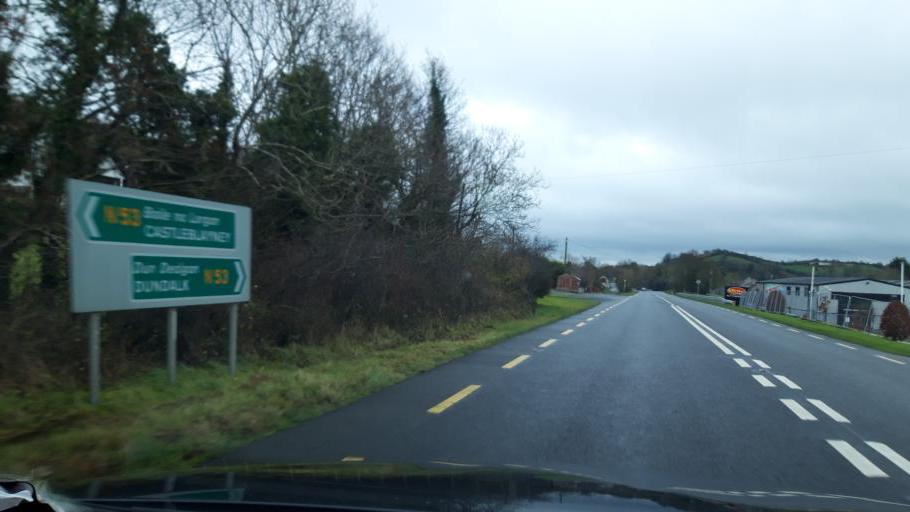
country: IE
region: Ulster
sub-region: County Monaghan
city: Castleblayney
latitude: 54.0929
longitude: -6.7000
